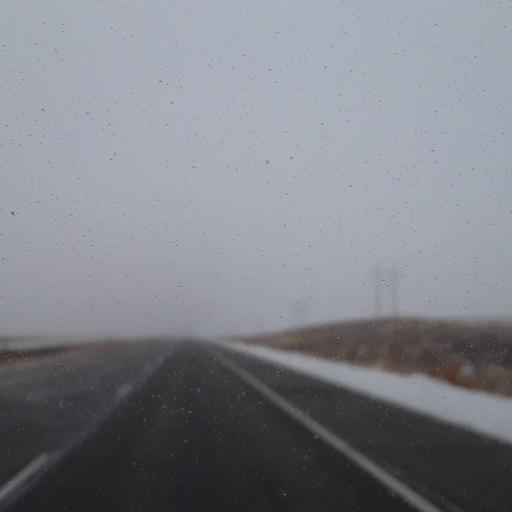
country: US
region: Nebraska
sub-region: Cheyenne County
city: Sidney
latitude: 40.7988
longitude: -102.8713
